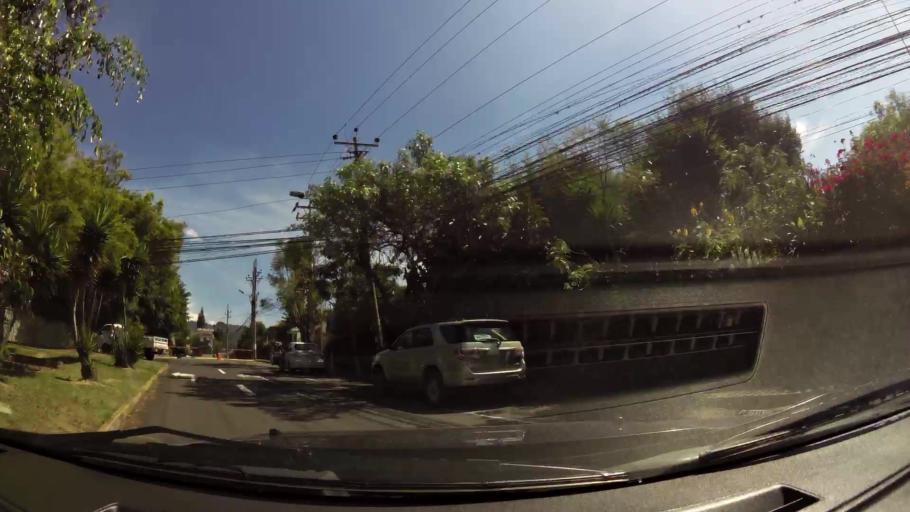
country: EC
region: Pichincha
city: Quito
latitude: -0.1953
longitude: -78.4332
